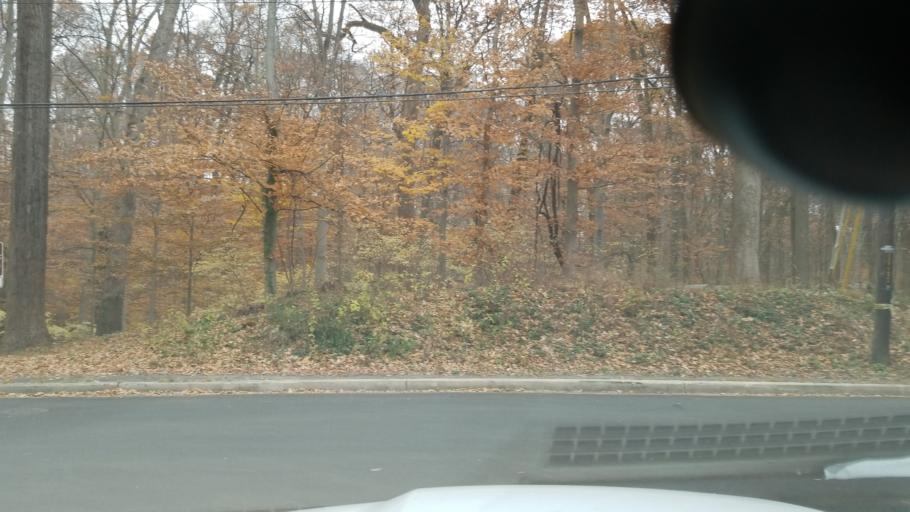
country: US
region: Maryland
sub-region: Montgomery County
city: Friendship Village
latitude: 38.9255
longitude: -77.0862
